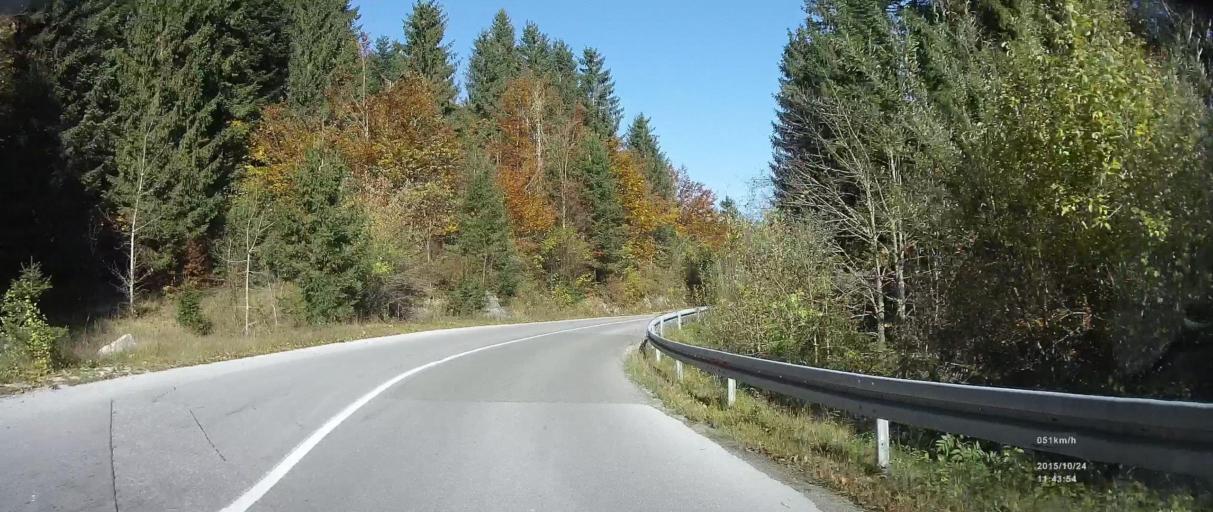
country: SI
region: Osilnica
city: Osilnica
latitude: 45.4362
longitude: 14.7088
